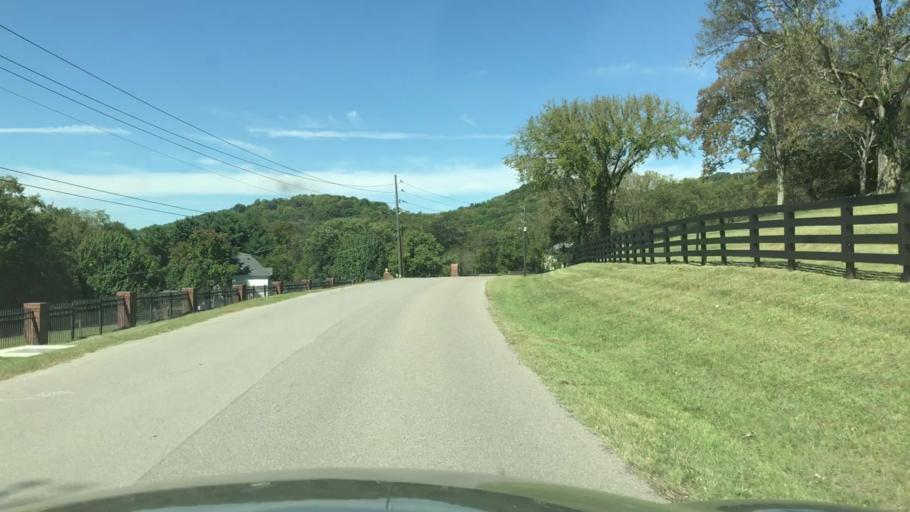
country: US
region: Tennessee
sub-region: Williamson County
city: Franklin
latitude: 35.9949
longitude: -86.8493
